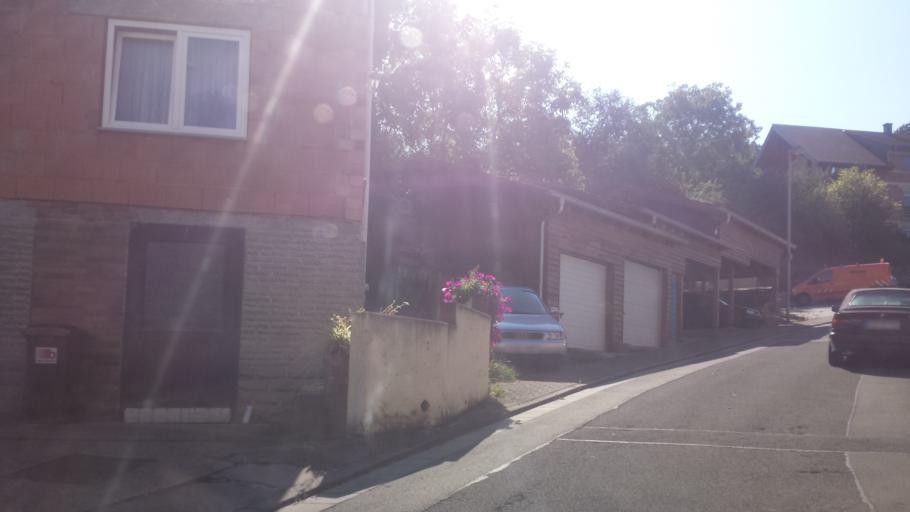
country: DE
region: Rheinland-Pfalz
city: Ramsen
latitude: 49.5358
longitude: 8.0121
